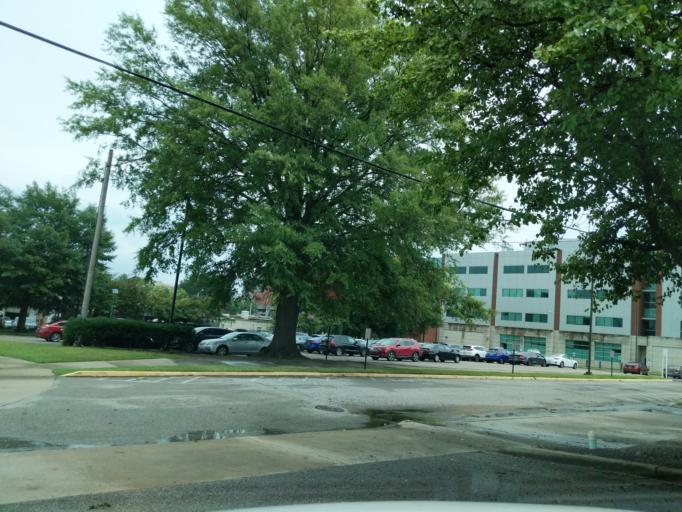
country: US
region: Tennessee
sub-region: Shelby County
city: Memphis
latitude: 35.1398
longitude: -90.0373
